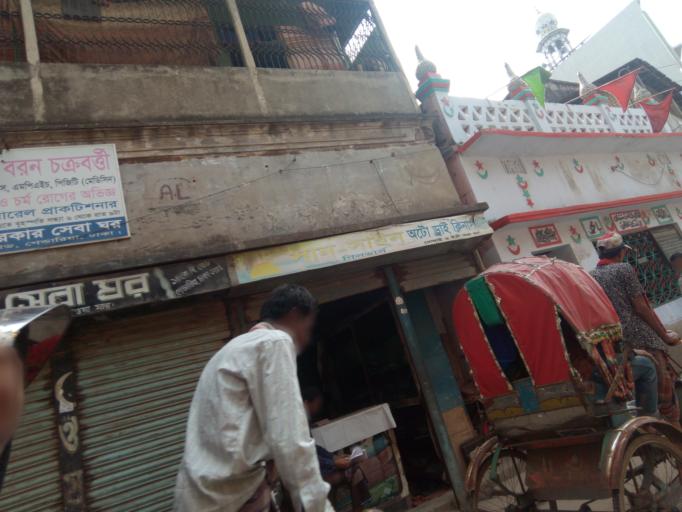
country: BD
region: Dhaka
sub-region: Dhaka
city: Dhaka
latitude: 23.7017
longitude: 90.4205
